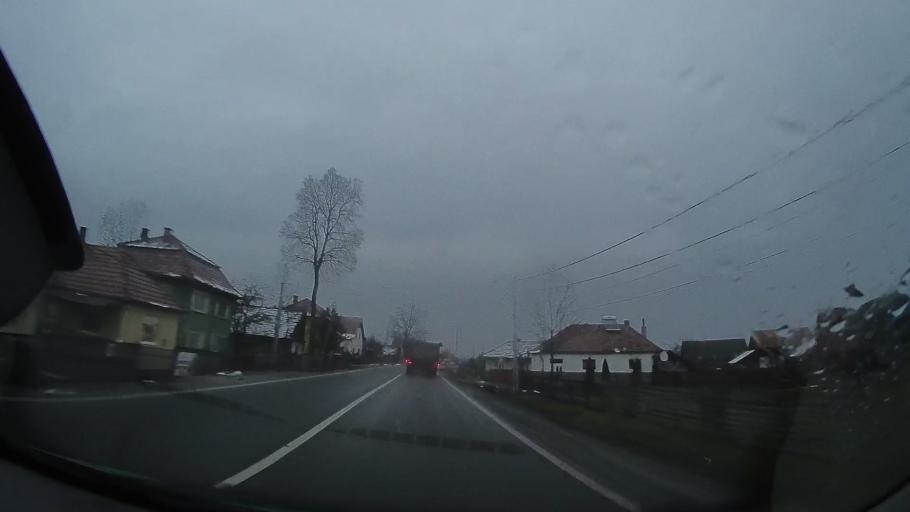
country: RO
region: Harghita
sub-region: Comuna Lazarea
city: Lazarea
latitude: 46.7570
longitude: 25.5177
